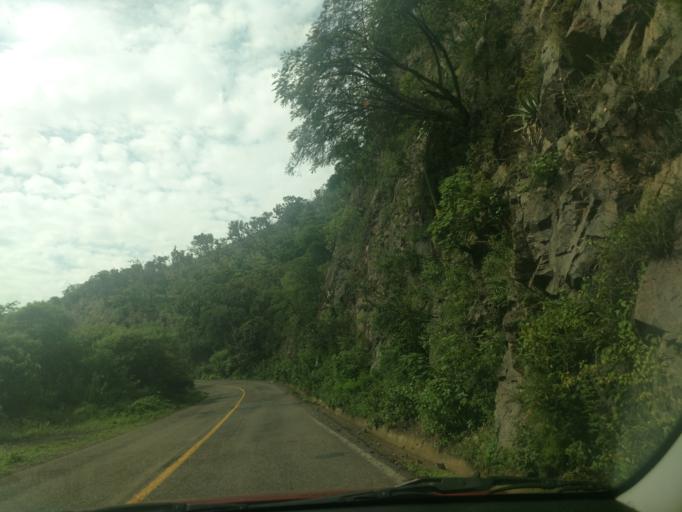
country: MX
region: Jalisco
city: El Salto
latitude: 20.3680
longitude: -104.5841
